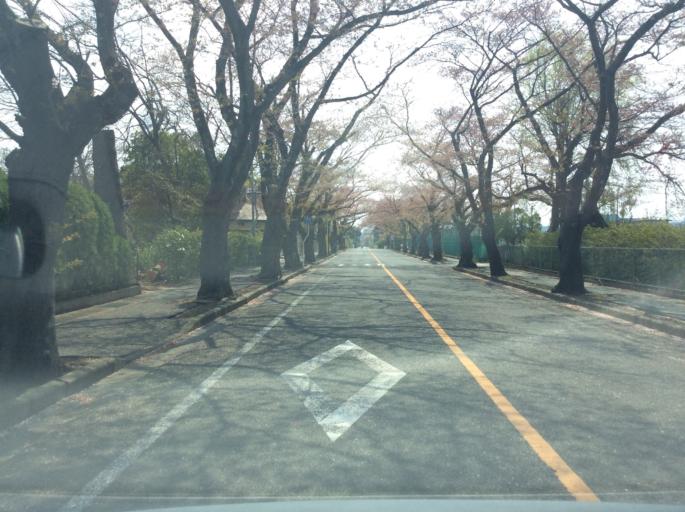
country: JP
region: Fukushima
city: Namie
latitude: 37.3597
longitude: 140.9960
